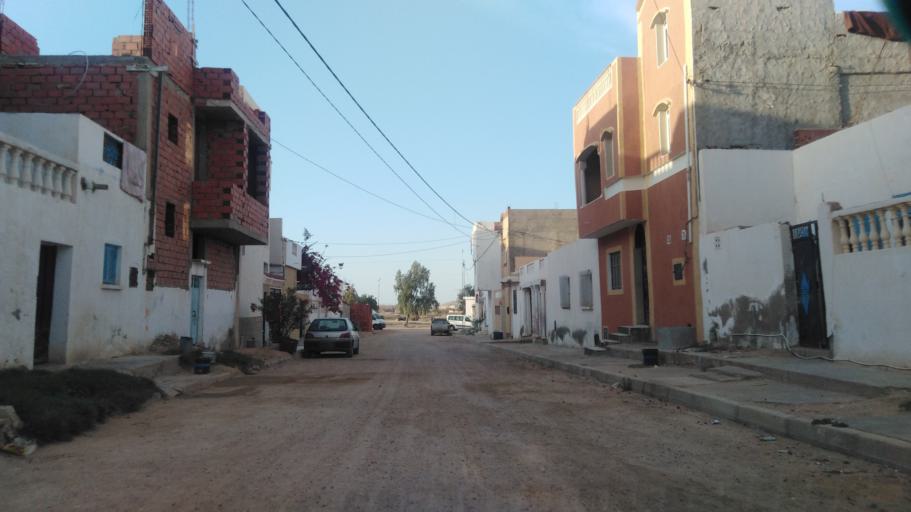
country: TN
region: Tataouine
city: Tataouine
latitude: 32.9425
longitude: 10.4579
